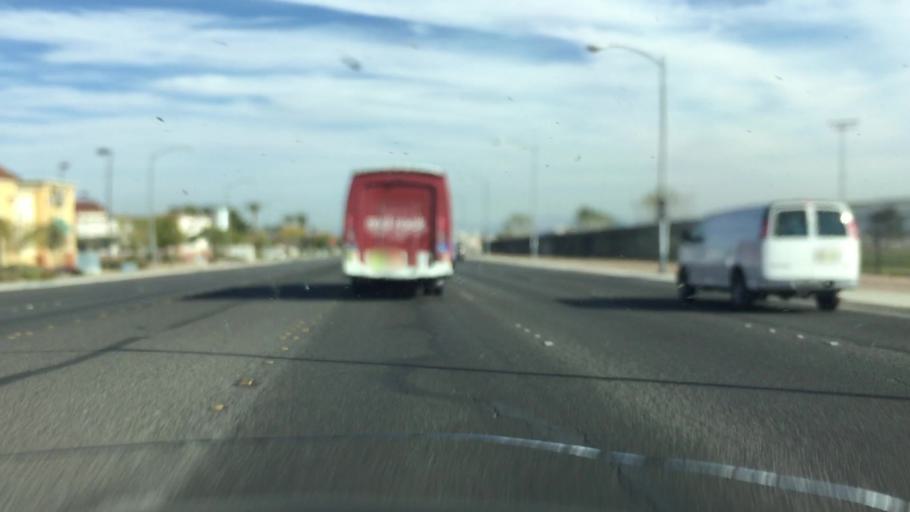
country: US
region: Nevada
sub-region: Clark County
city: Spring Valley
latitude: 36.1293
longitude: -115.2760
